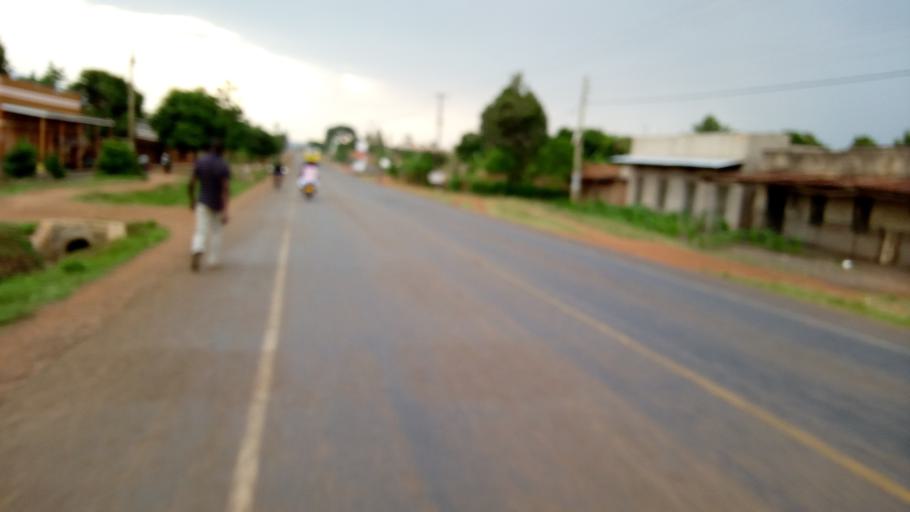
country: UG
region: Eastern Region
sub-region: Mbale District
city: Mbale
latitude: 1.1377
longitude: 34.1653
